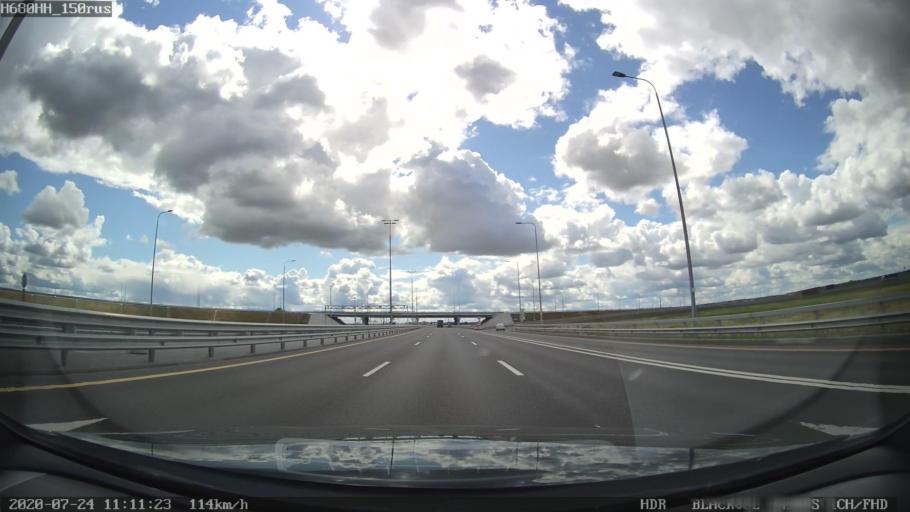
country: RU
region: St.-Petersburg
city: Tyarlevo
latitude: 59.7236
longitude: 30.5146
